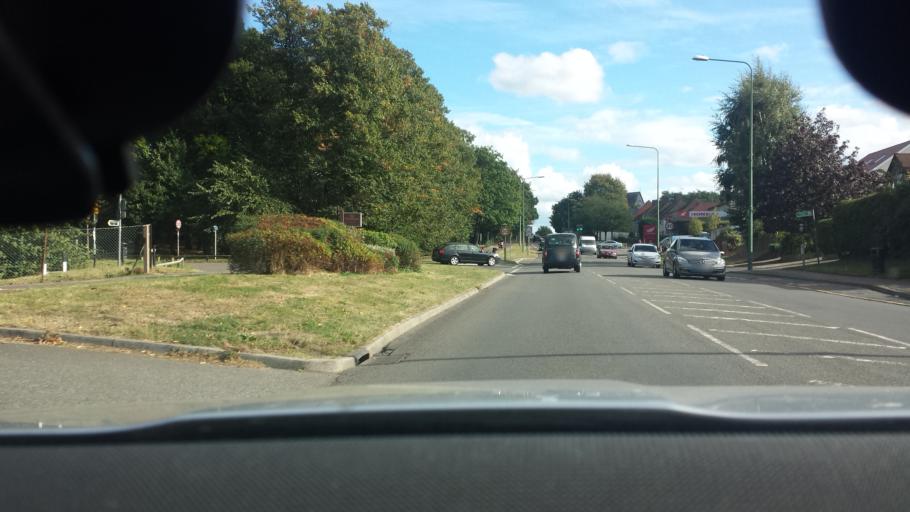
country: GB
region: England
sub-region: Kent
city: Swanley
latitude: 51.3999
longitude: 0.1684
